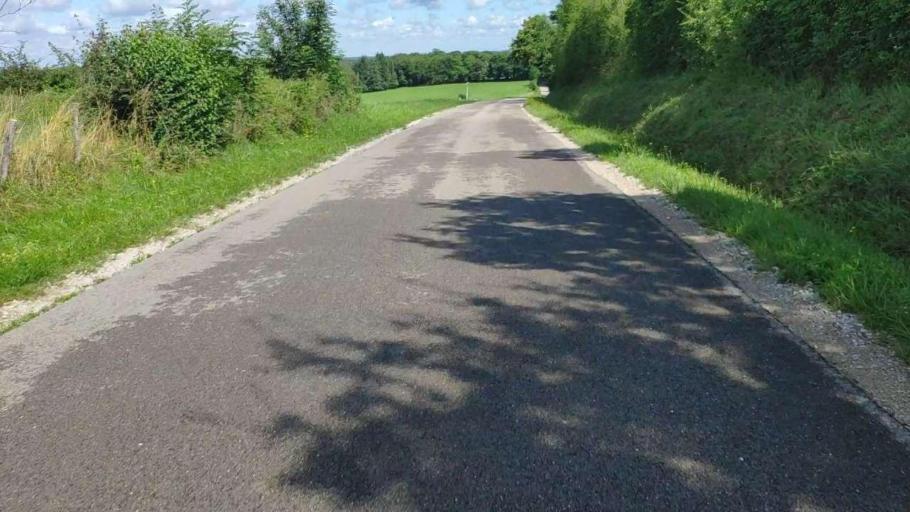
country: FR
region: Franche-Comte
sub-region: Departement du Jura
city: Bletterans
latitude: 46.8118
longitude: 5.5613
